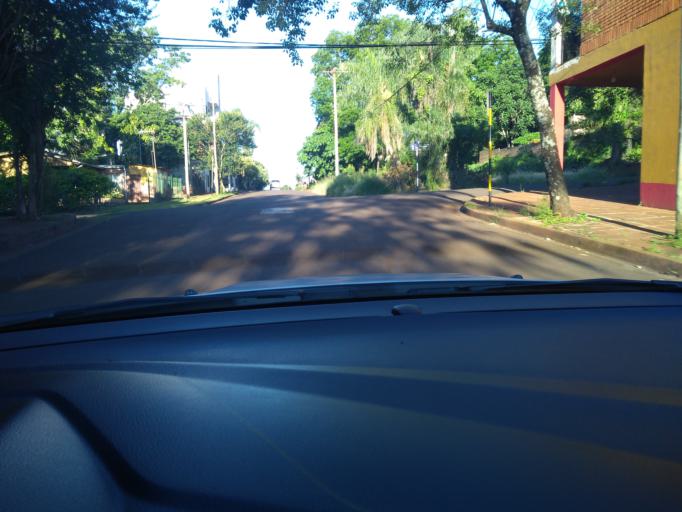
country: AR
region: Misiones
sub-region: Departamento de Obera
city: Obera
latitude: -27.4814
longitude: -55.1145
